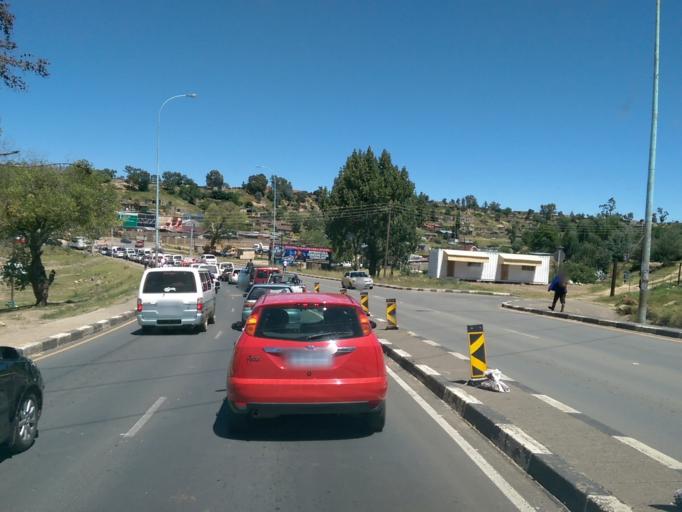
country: LS
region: Maseru
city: Maseru
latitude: -29.3303
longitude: 27.5045
